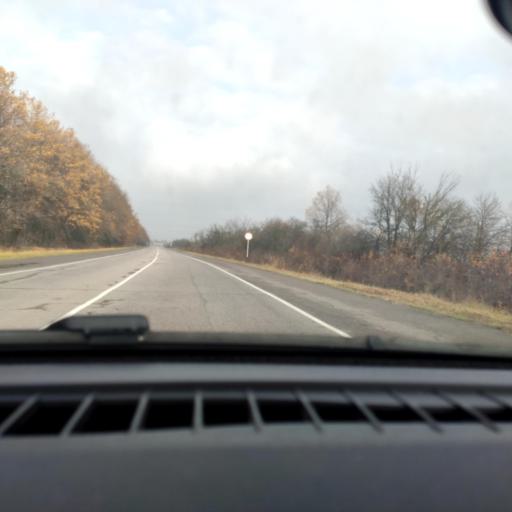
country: RU
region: Voronezj
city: Kolodeznyy
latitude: 51.3248
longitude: 39.0277
